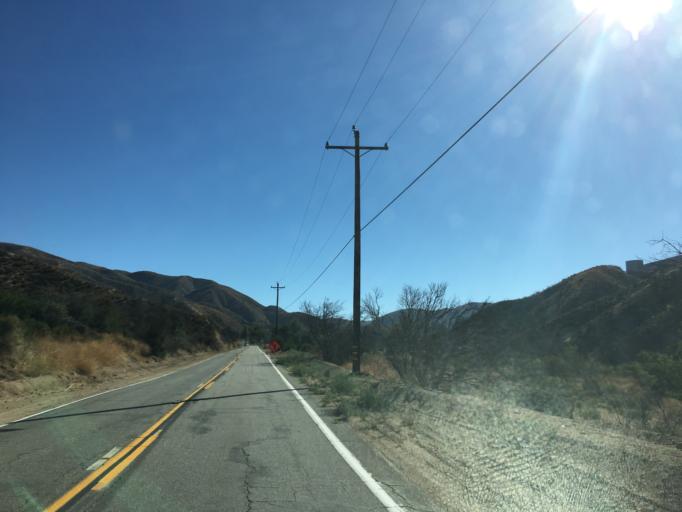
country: US
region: California
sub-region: Los Angeles County
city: Green Valley
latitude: 34.6498
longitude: -118.4854
